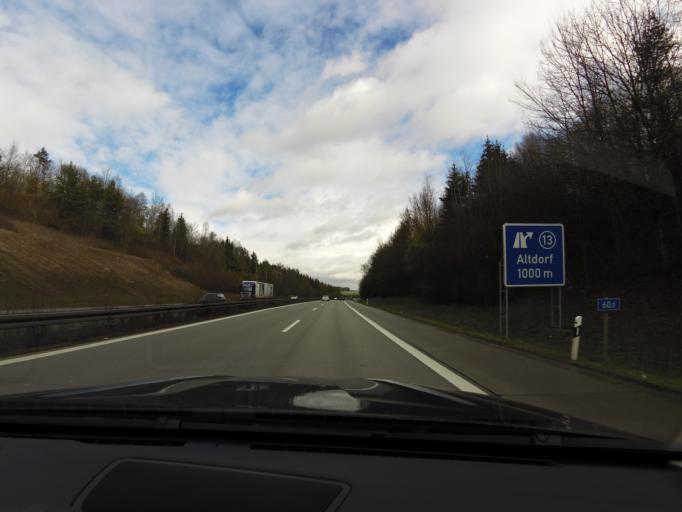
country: DE
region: Bavaria
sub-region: Lower Bavaria
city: Weihmichl
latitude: 48.5598
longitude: 12.0798
